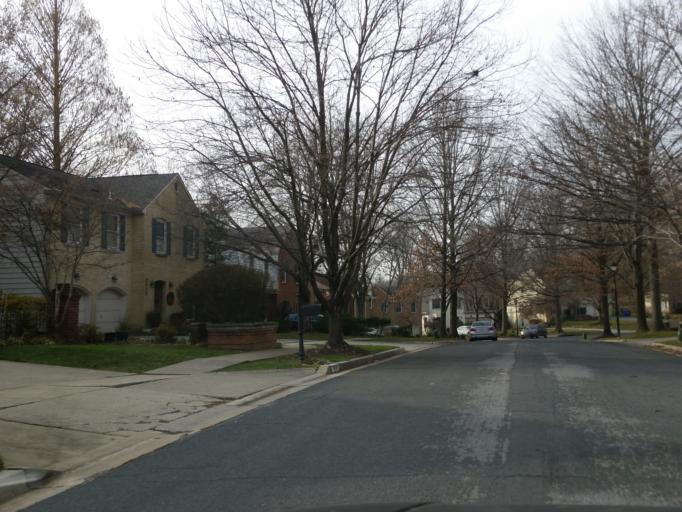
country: US
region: Maryland
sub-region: Montgomery County
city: Forest Glen
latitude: 38.9896
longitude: -77.0538
